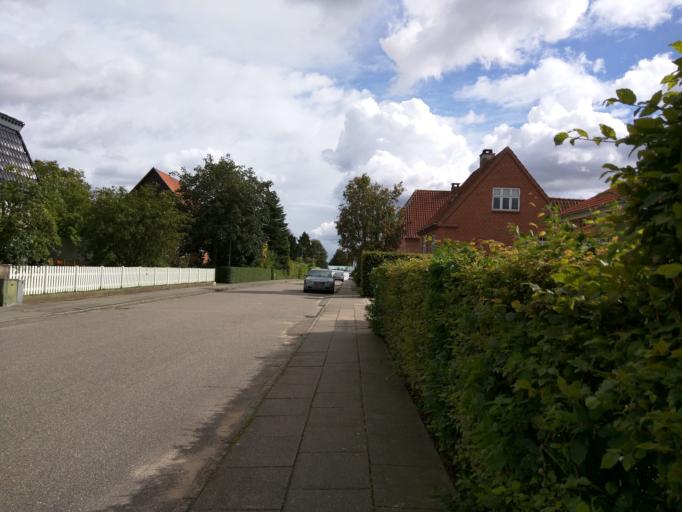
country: DK
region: Central Jutland
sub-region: Viborg Kommune
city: Viborg
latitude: 56.4596
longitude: 9.4061
